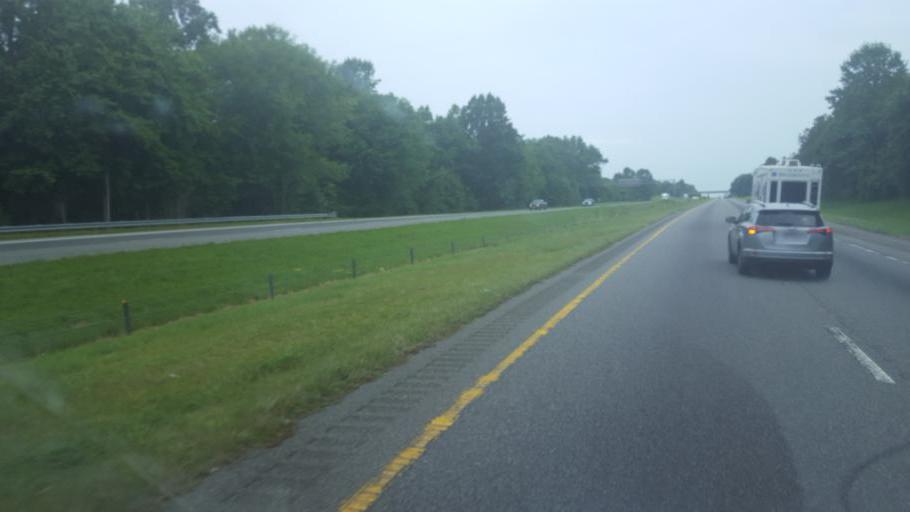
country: US
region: North Carolina
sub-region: Iredell County
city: Statesville
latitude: 35.8623
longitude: -80.8642
